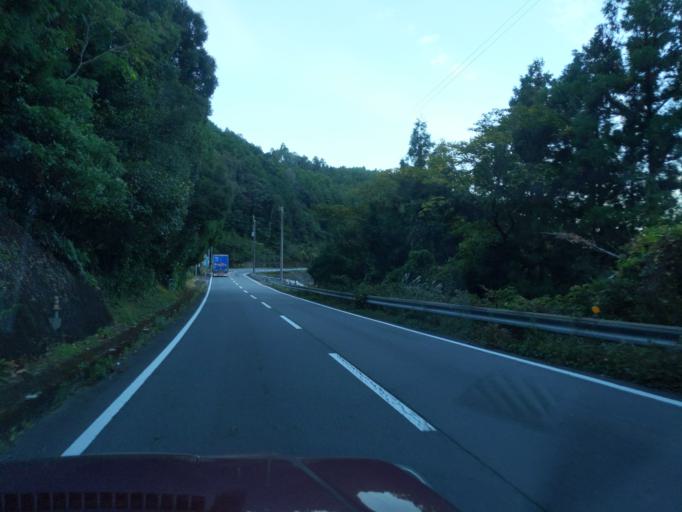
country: JP
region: Tokushima
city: Anan
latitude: 33.7013
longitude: 134.4437
